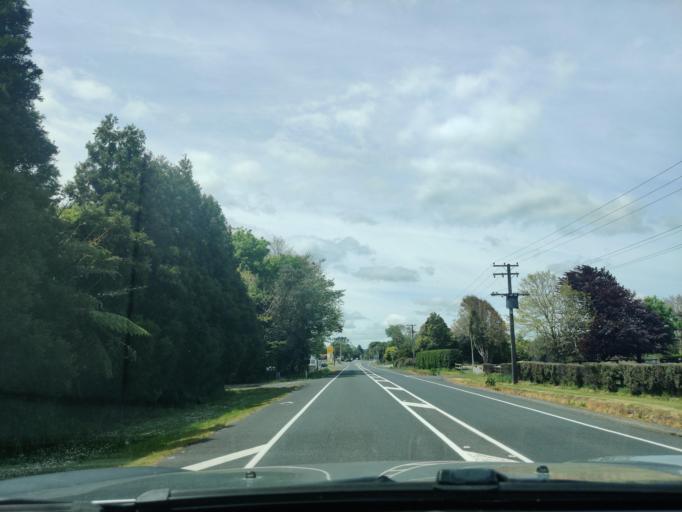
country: NZ
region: Taranaki
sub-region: New Plymouth District
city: New Plymouth
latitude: -39.1440
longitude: 174.1423
